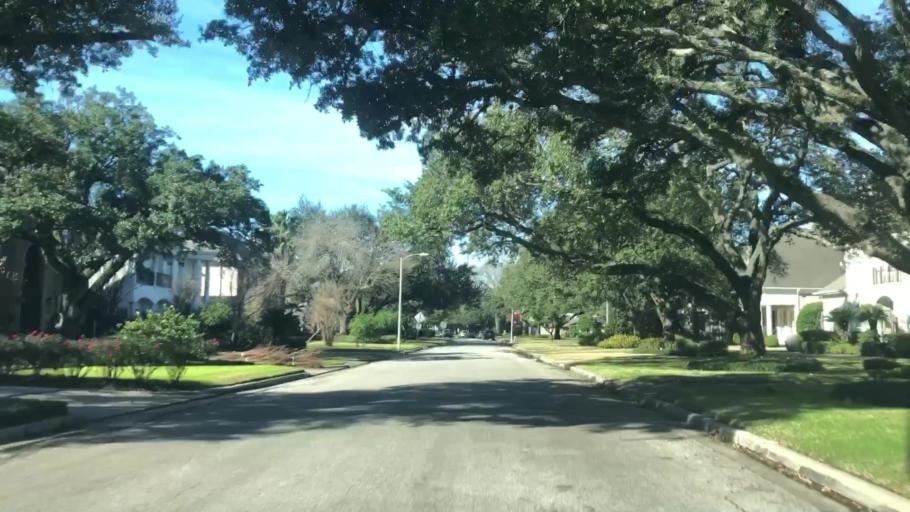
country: US
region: Texas
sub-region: Harris County
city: Hunters Creek Village
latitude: 29.7535
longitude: -95.4663
